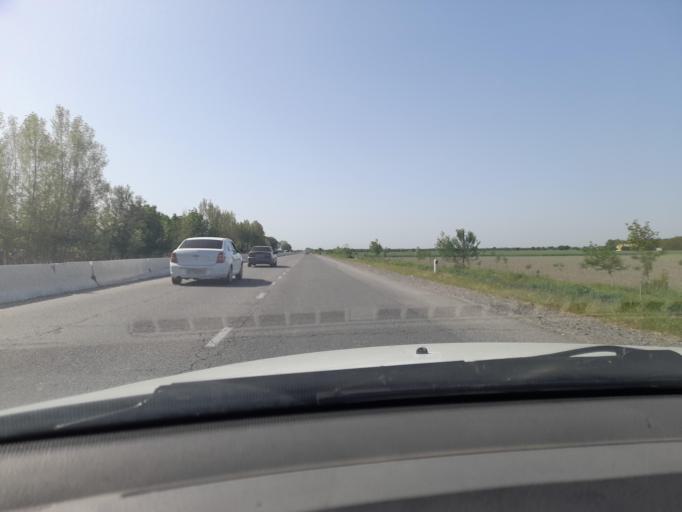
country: UZ
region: Samarqand
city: Daxbet
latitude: 39.8173
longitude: 66.8486
